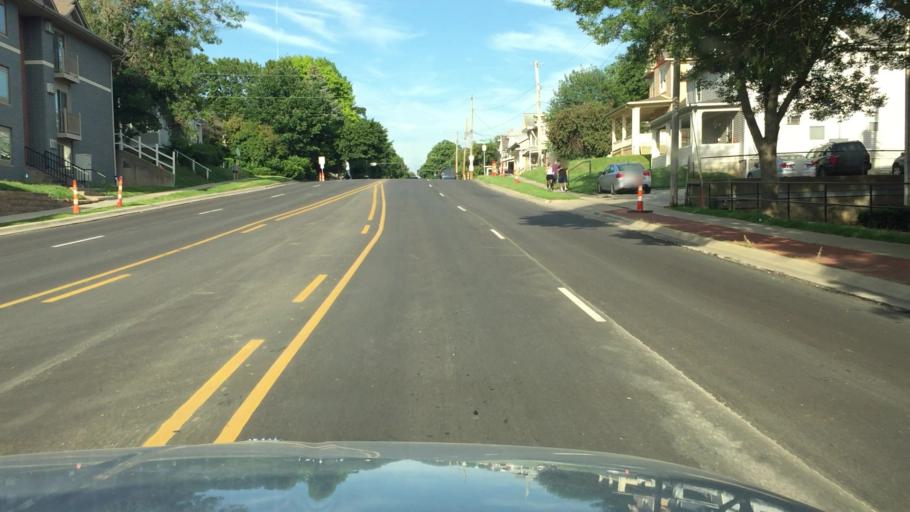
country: US
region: Iowa
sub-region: Johnson County
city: Iowa City
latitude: 41.6578
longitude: -91.5283
